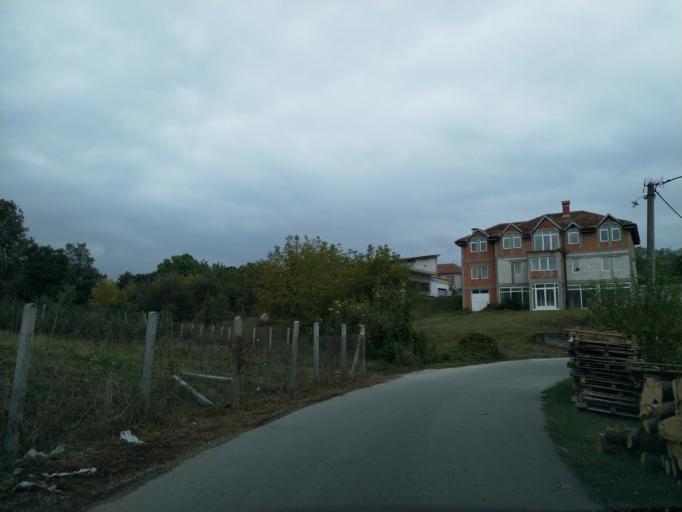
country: RS
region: Central Serbia
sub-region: Sumadijski Okrug
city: Arangelovac
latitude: 44.3037
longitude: 20.5869
